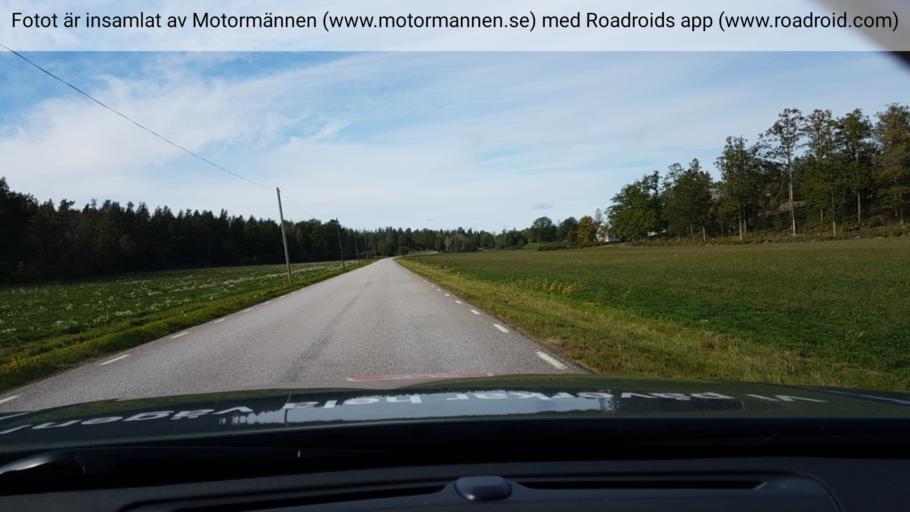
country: SE
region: OEstergoetland
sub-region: Valdemarsviks Kommun
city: Valdemarsvik
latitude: 58.1240
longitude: 16.6360
